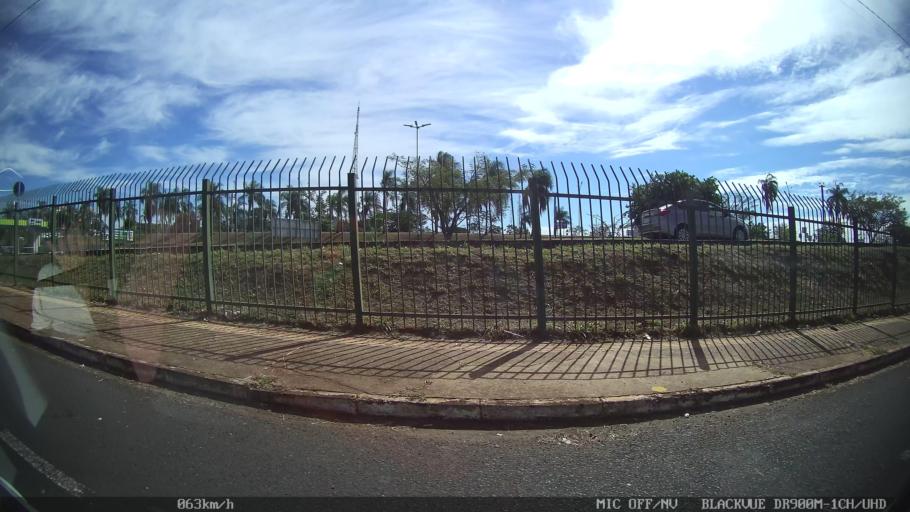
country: BR
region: Sao Paulo
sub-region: Sao Jose Do Rio Preto
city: Sao Jose do Rio Preto
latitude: -20.8343
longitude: -49.3549
